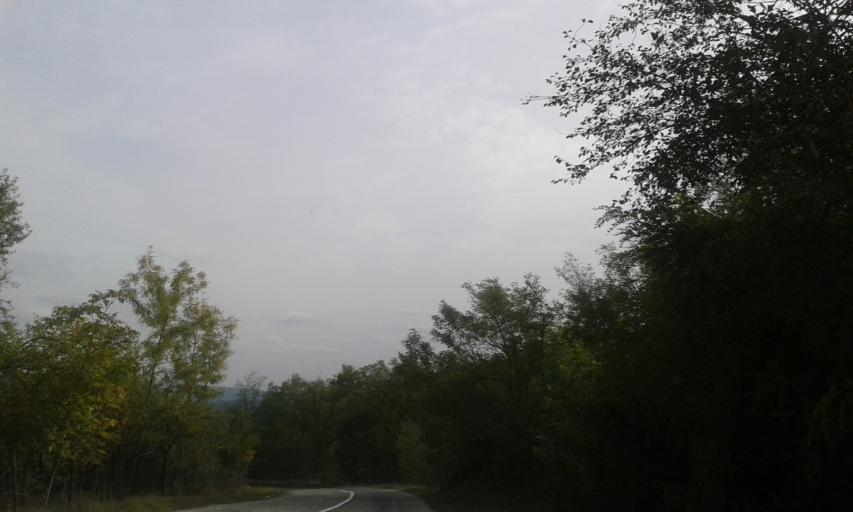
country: RO
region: Gorj
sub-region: Comuna Bustuchin
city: Bustuchin
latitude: 44.9155
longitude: 23.7729
